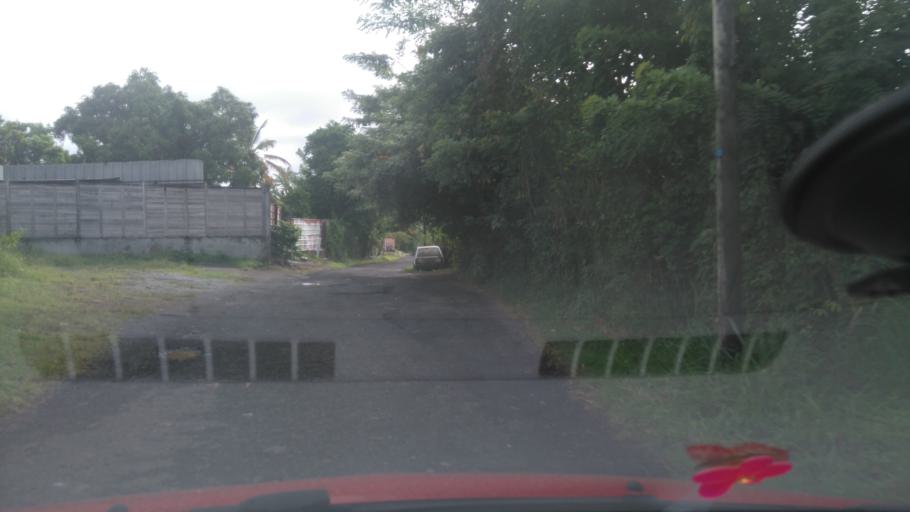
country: MQ
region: Martinique
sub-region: Martinique
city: Ducos
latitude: 14.5525
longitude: -60.9626
